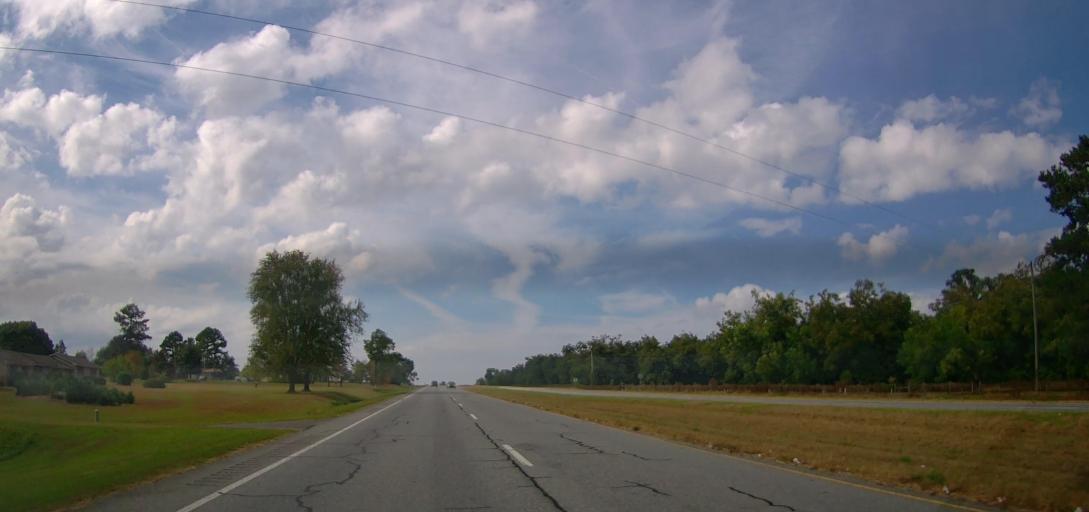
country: US
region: Georgia
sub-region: Thomas County
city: Meigs
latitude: 31.1057
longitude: -84.1120
